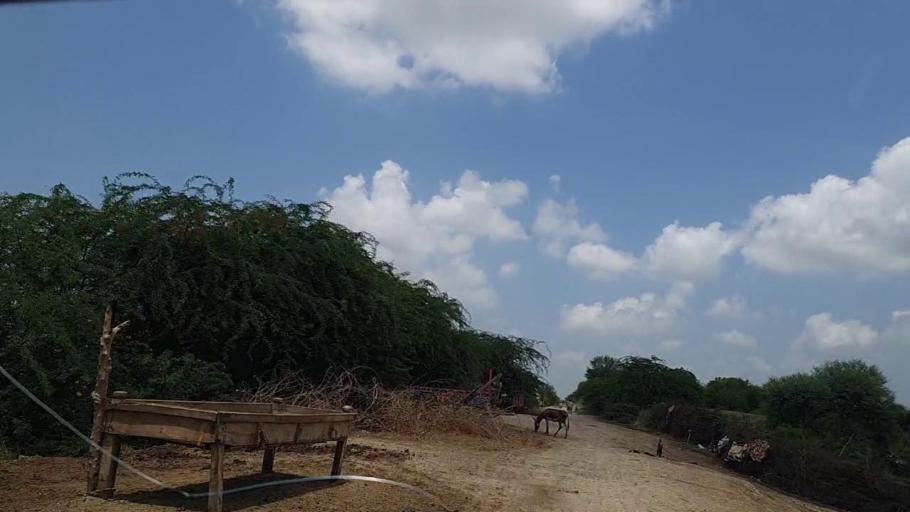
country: PK
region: Sindh
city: Tharu Shah
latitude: 26.9583
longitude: 68.0273
